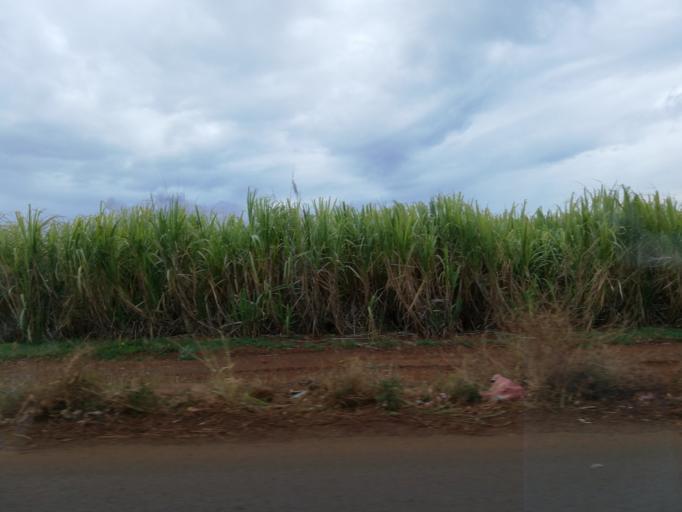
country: MU
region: Black River
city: Petite Riviere
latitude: -20.2112
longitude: 57.4552
